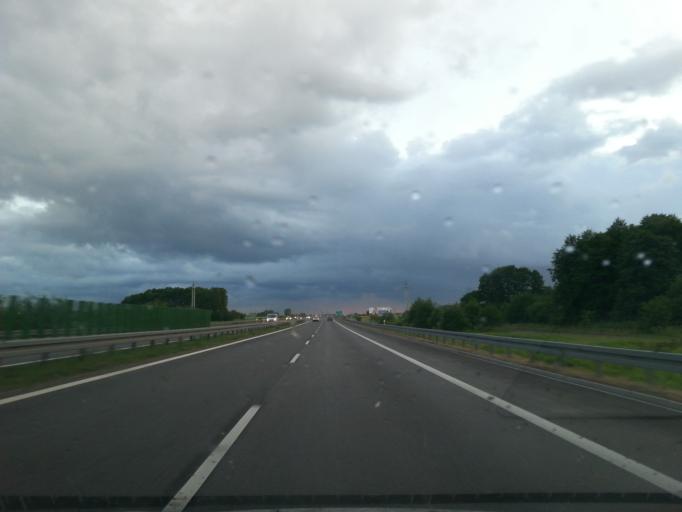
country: PL
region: Lower Silesian Voivodeship
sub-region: Powiat olesnicki
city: Olesnica
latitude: 51.2334
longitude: 17.3913
